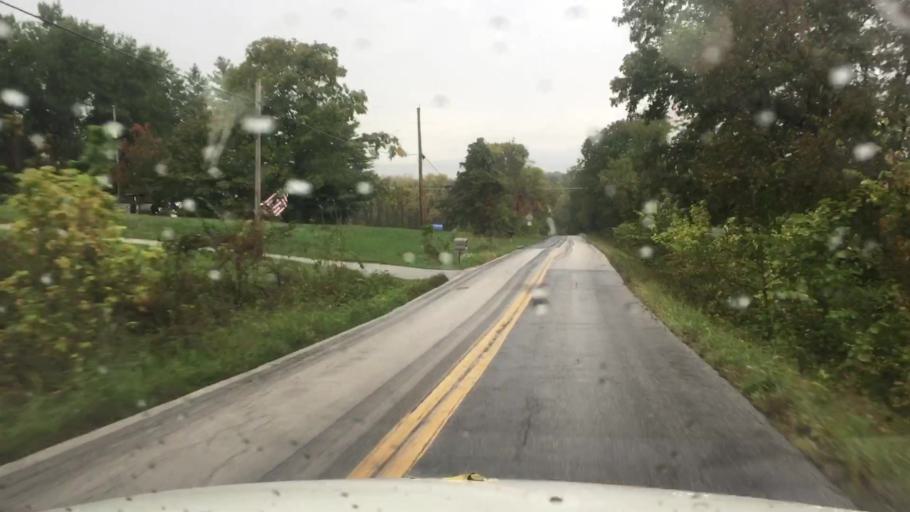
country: US
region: Missouri
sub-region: Boone County
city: Columbia
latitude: 38.9345
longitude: -92.4965
